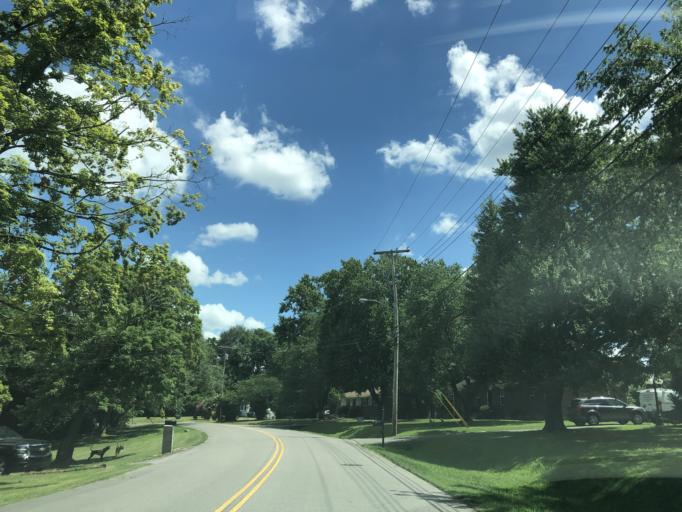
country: US
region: Tennessee
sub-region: Davidson County
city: Oak Hill
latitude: 36.0766
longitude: -86.7187
